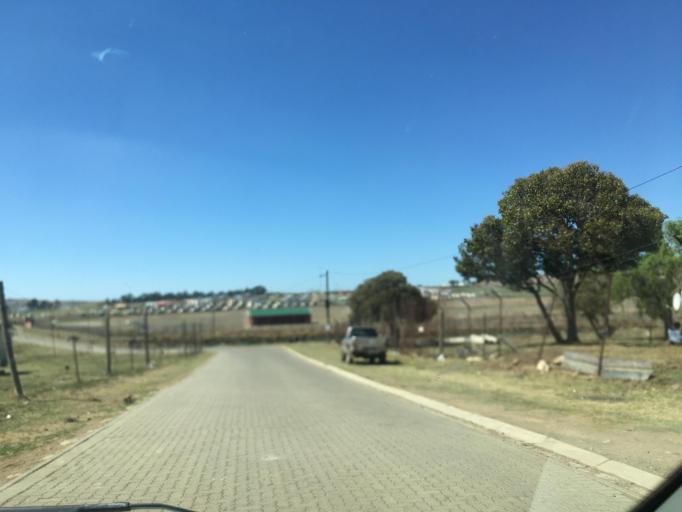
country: ZA
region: Eastern Cape
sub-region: Chris Hani District Municipality
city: Elliot
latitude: -31.3305
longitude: 27.8266
